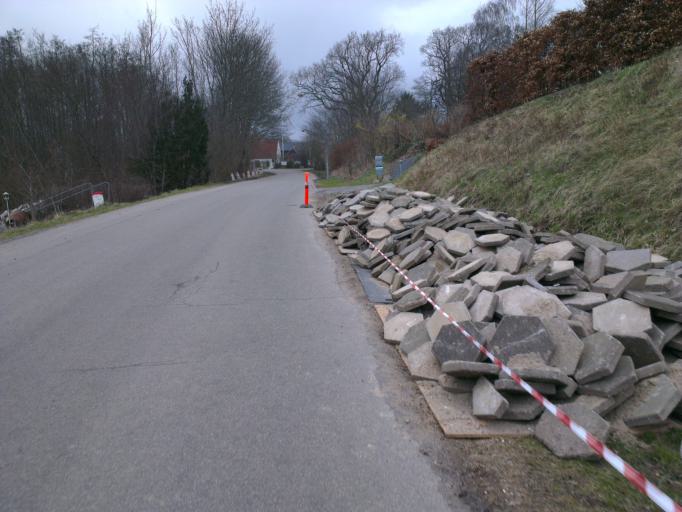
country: DK
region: Capital Region
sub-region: Frederikssund Kommune
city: Frederikssund
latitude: 55.8814
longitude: 12.0702
